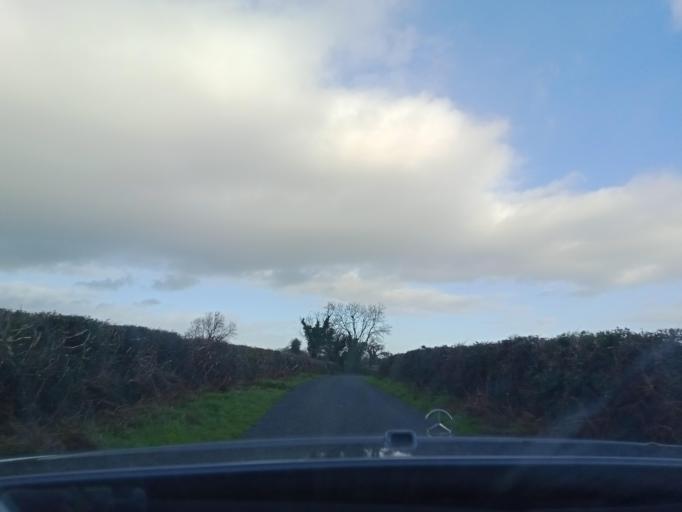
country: IE
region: Leinster
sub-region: Kilkenny
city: Callan
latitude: 52.4730
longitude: -7.3830
